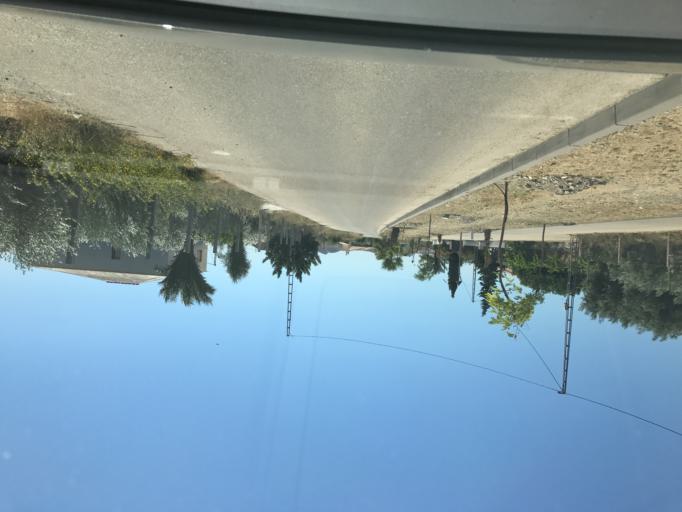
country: ES
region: Andalusia
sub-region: Provincia de Almeria
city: Fines
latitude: 37.3561
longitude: -2.2547
